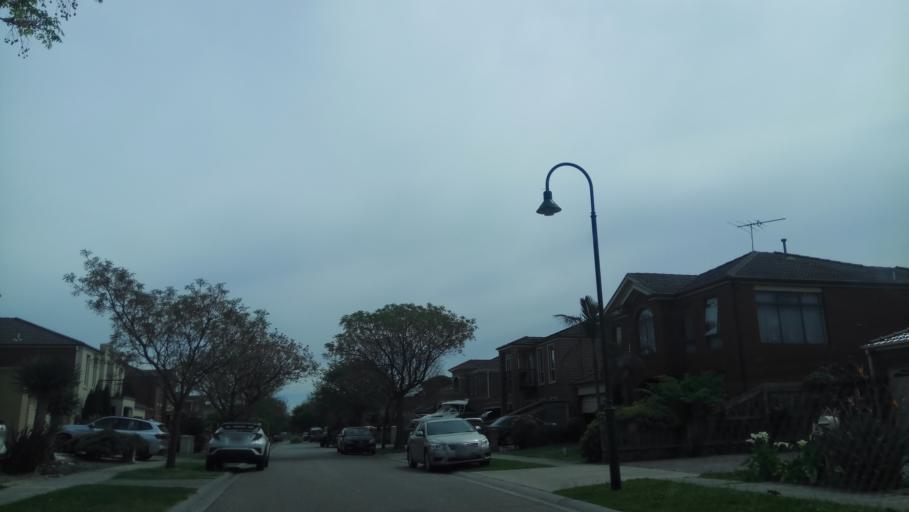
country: AU
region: Victoria
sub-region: Kingston
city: Dingley Village
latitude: -37.9672
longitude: 145.1298
